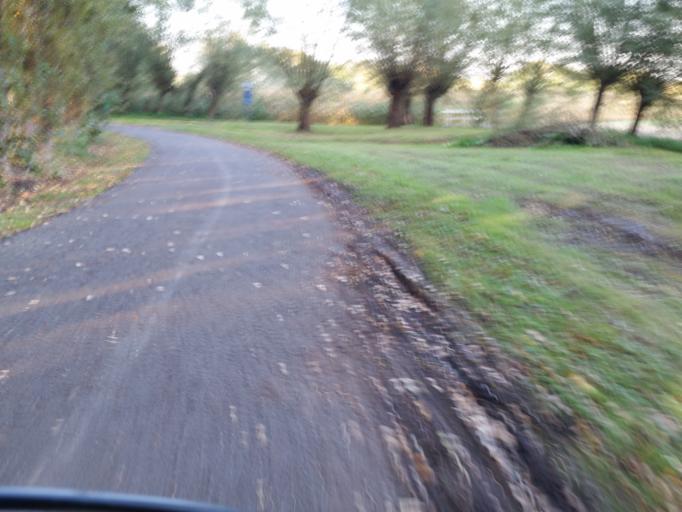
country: BE
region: Flanders
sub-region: Provincie Antwerpen
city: Schelle
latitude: 51.1247
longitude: 4.3255
